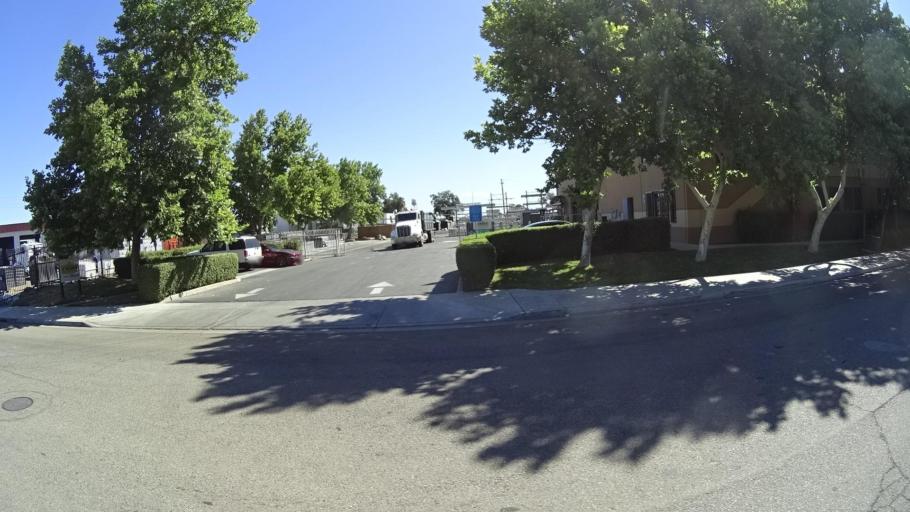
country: US
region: California
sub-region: Fresno County
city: Fresno
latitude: 36.7127
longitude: -119.7767
